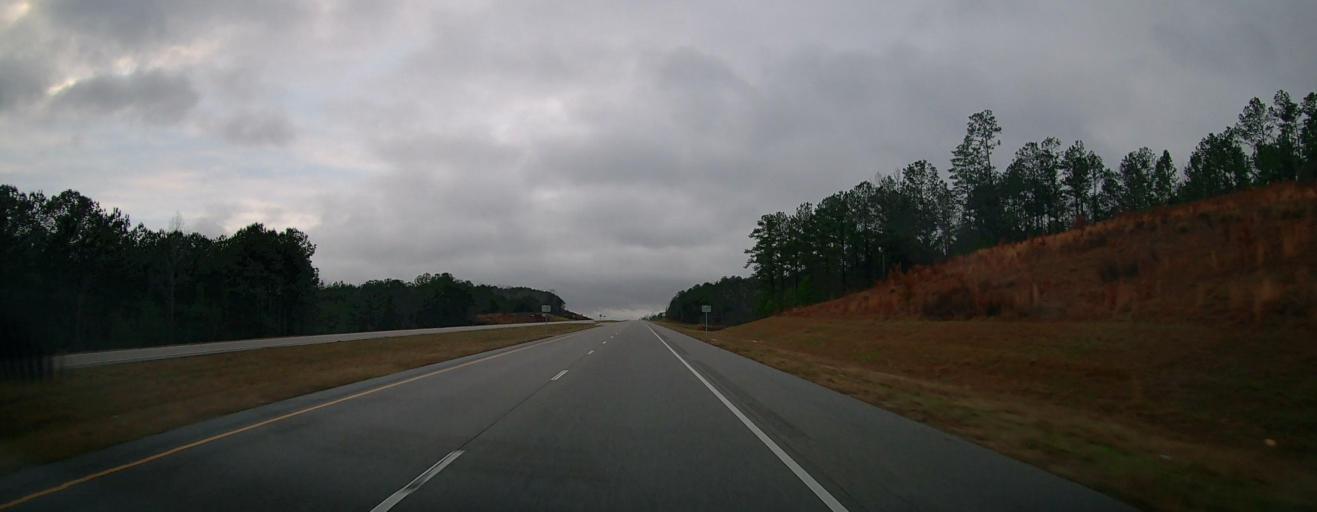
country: US
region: Alabama
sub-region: Bibb County
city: Centreville
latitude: 32.9499
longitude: -87.1038
